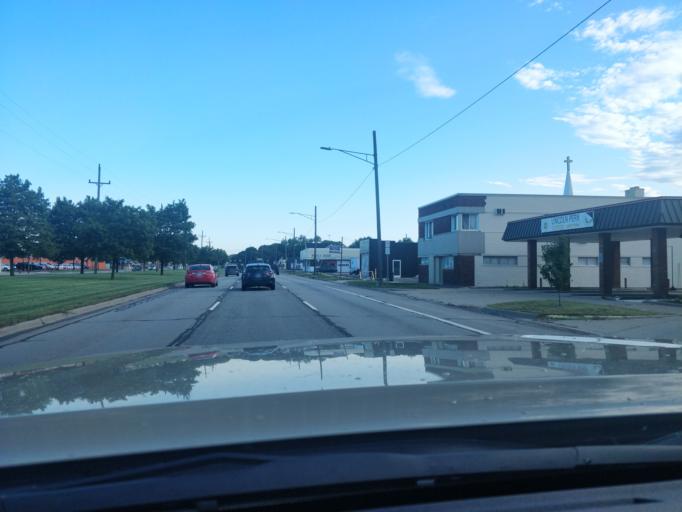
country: US
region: Michigan
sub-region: Wayne County
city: Lincoln Park
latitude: 42.2346
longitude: -83.1800
